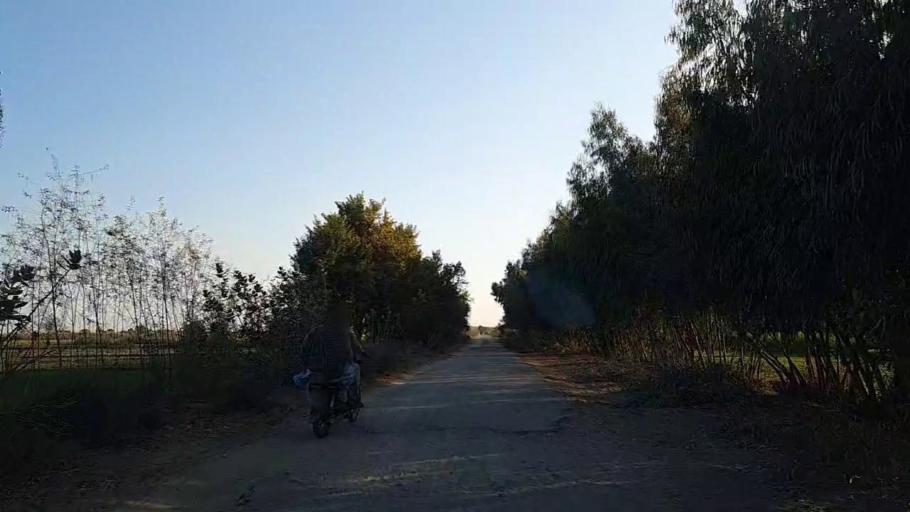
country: PK
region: Sindh
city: Khadro
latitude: 26.2745
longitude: 68.8100
